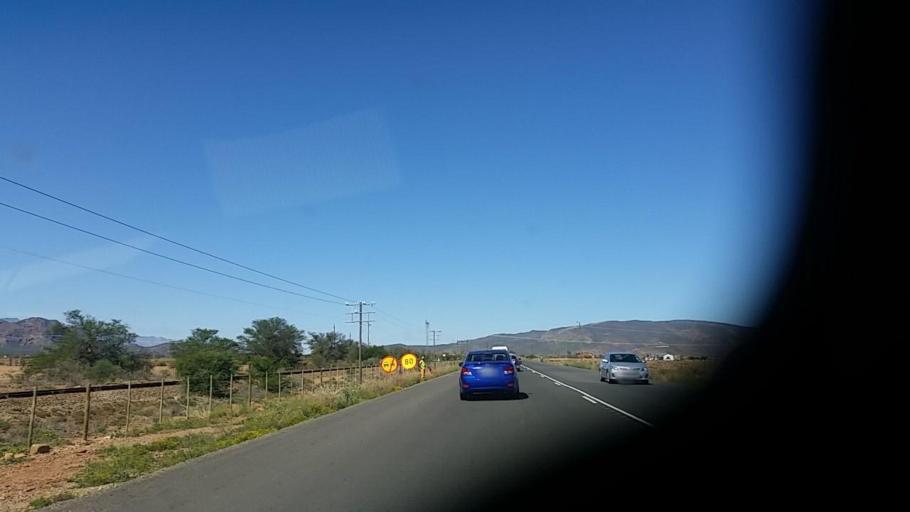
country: ZA
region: Western Cape
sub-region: Eden District Municipality
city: Oudtshoorn
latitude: -33.5608
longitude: 22.3890
